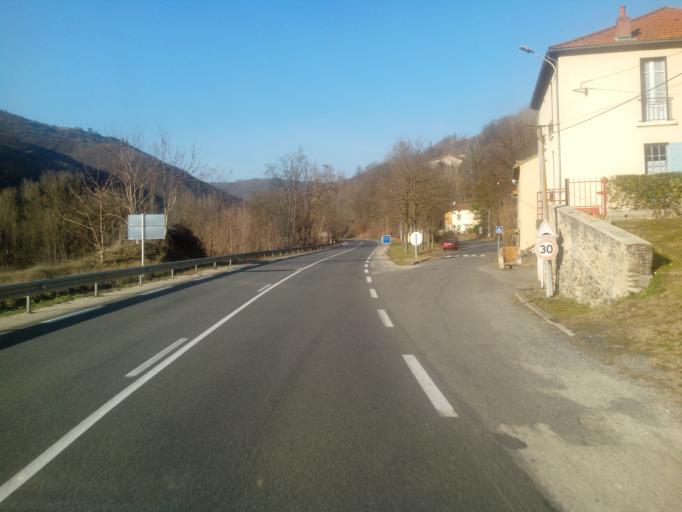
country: FR
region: Midi-Pyrenees
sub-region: Departement de l'Aveyron
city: Viviez
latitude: 44.5642
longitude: 2.2135
